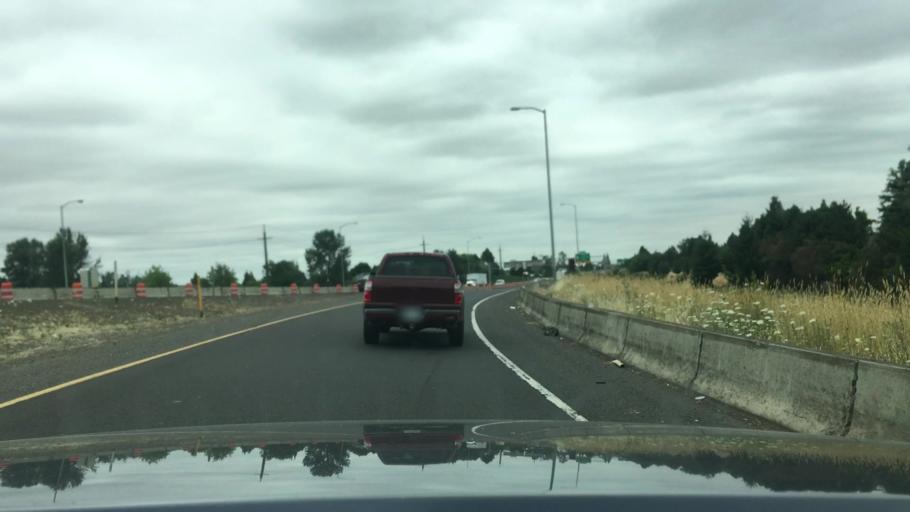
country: US
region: Oregon
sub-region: Lane County
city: Eugene
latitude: 44.0865
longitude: -123.1713
